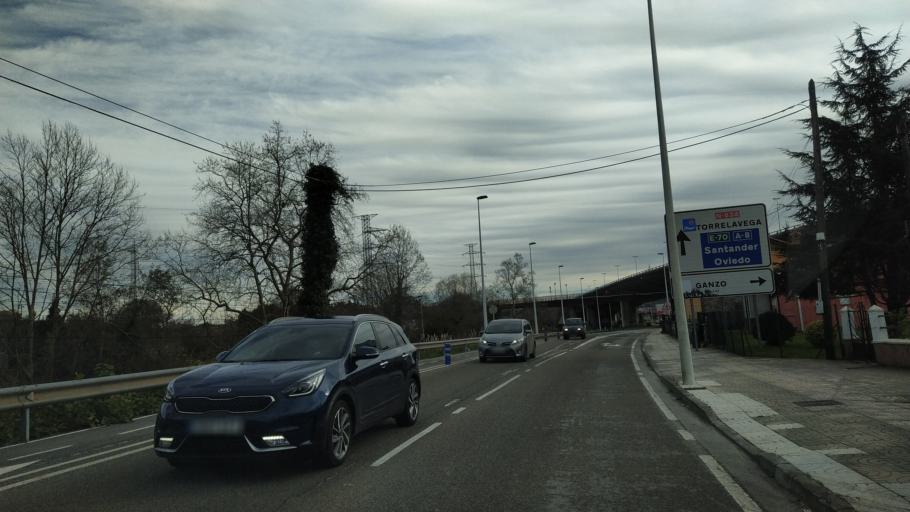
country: ES
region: Cantabria
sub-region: Provincia de Cantabria
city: Reocin
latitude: 43.3576
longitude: -4.0752
